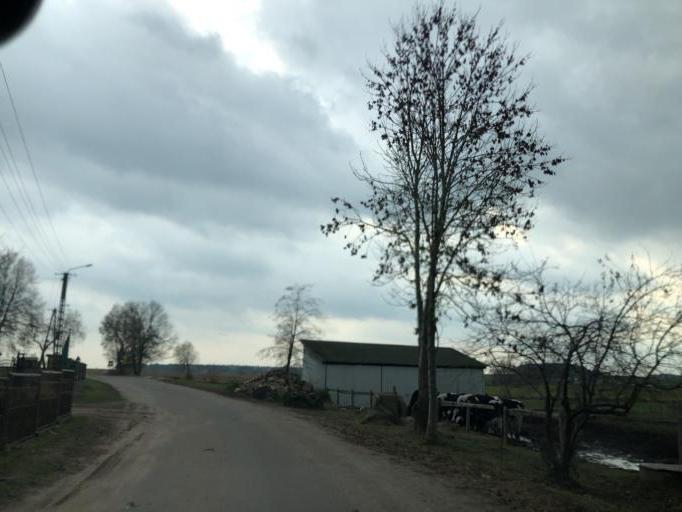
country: PL
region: Podlasie
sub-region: Lomza
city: Lomza
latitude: 53.1555
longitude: 22.0029
